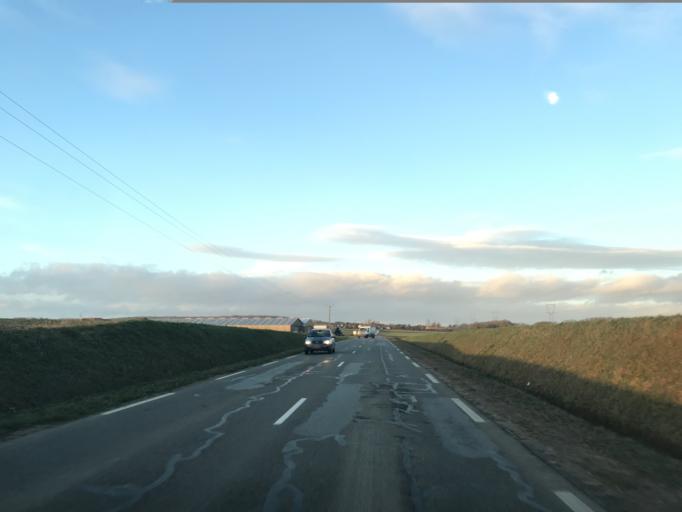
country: FR
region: Ile-de-France
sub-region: Departement des Yvelines
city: Galluis
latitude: 48.8254
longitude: 1.8202
